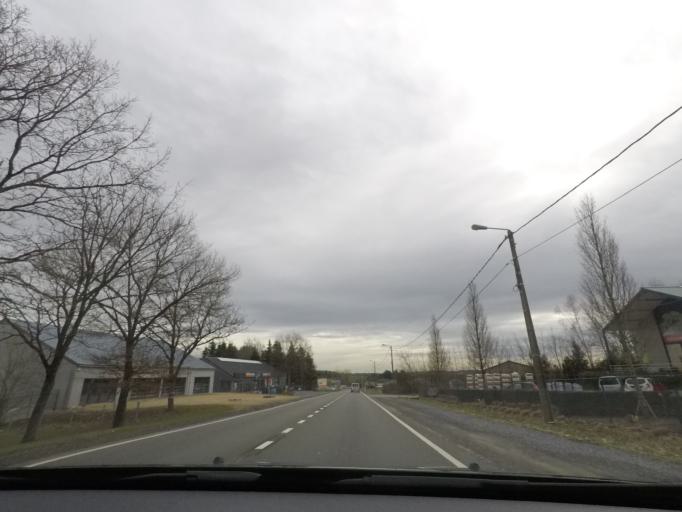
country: LU
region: Diekirch
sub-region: Canton de Wiltz
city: Winseler
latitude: 49.9837
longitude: 5.8328
